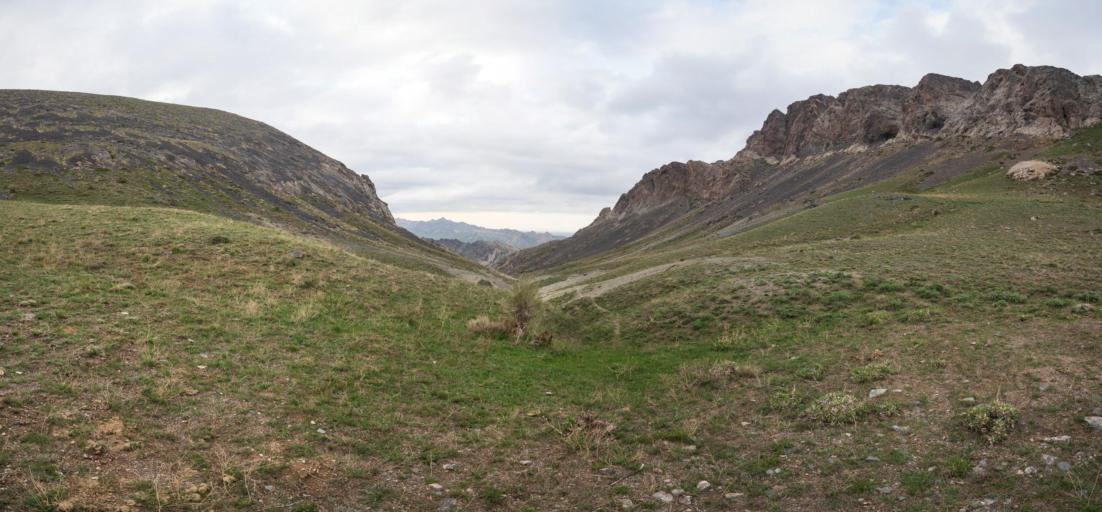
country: KZ
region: Ongtustik Qazaqstan
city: Ashchysay
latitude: 43.6583
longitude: 68.8788
